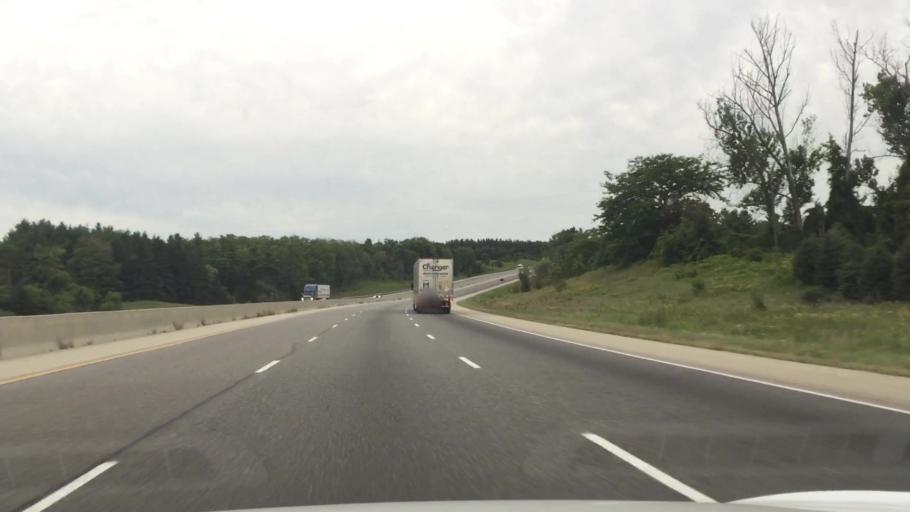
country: CA
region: Ontario
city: Kitchener
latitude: 43.2751
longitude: -80.5285
